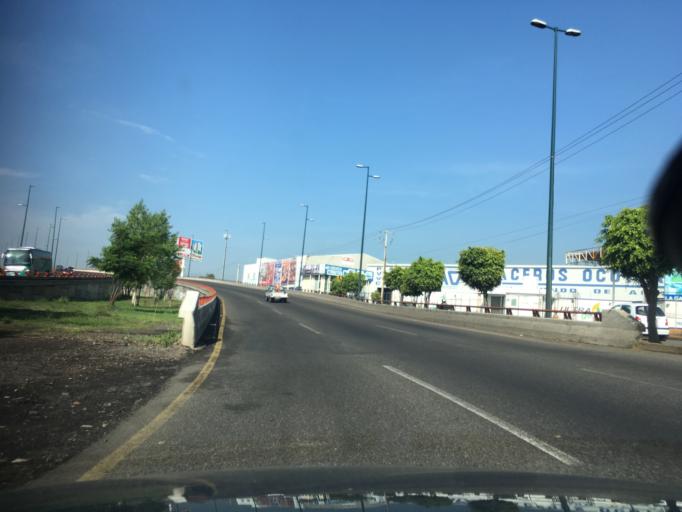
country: MX
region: Michoacan
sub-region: Tarimbaro
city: Fraccionamiento Metropolis II
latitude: 19.7274
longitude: -101.2221
